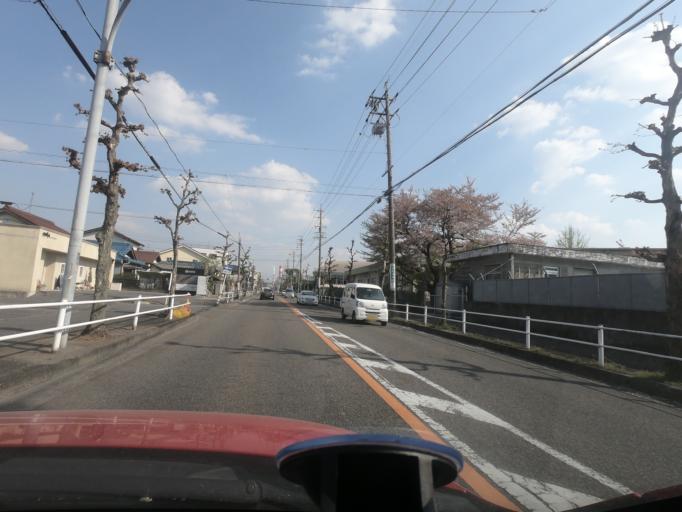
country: JP
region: Aichi
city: Kasugai
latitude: 35.2426
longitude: 136.9665
